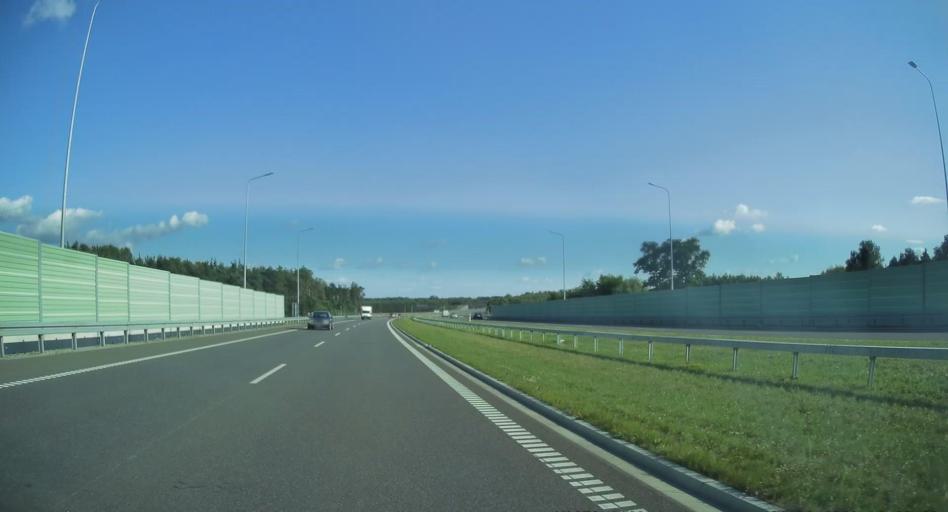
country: PL
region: Masovian Voivodeship
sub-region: Powiat radomski
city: Jedlinsk
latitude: 51.5300
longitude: 21.0814
